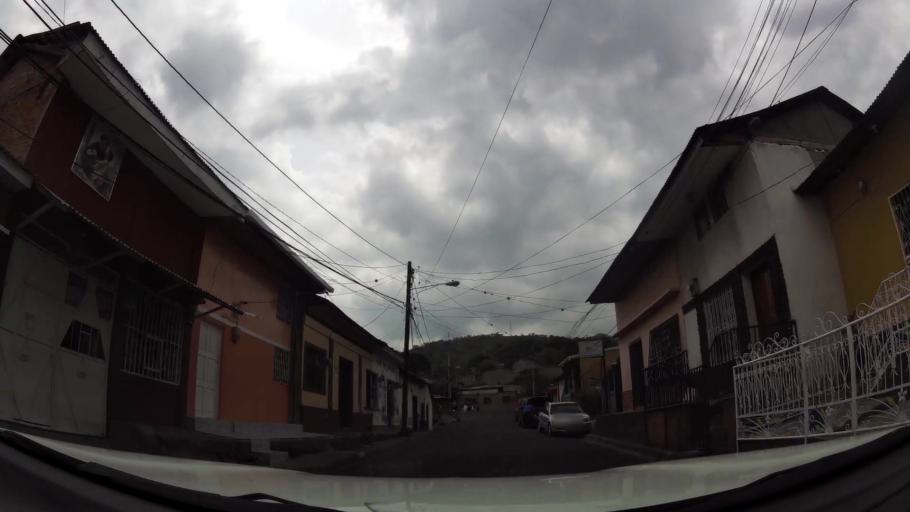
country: NI
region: Matagalpa
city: Matagalpa
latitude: 12.9243
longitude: -85.9170
